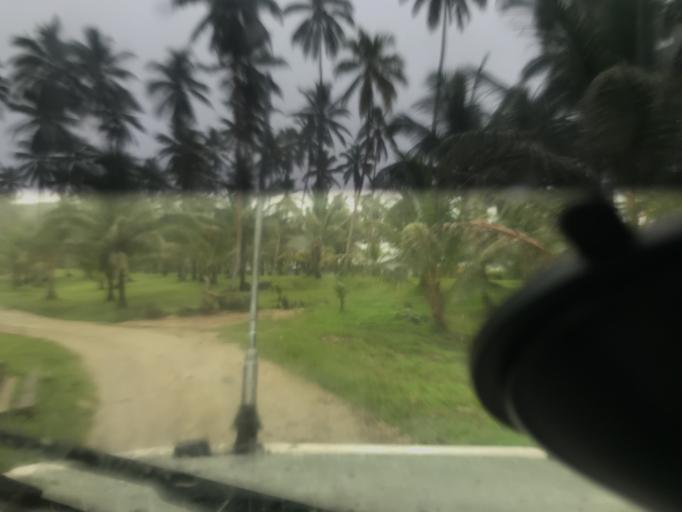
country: SB
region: Choiseul
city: Taro'a
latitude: -9.1940
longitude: 160.9508
